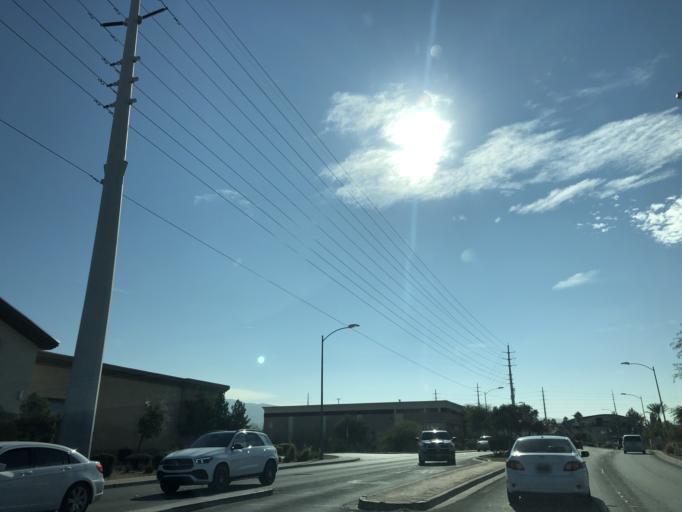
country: US
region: Nevada
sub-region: Clark County
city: Whitney
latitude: 36.0606
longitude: -115.0366
